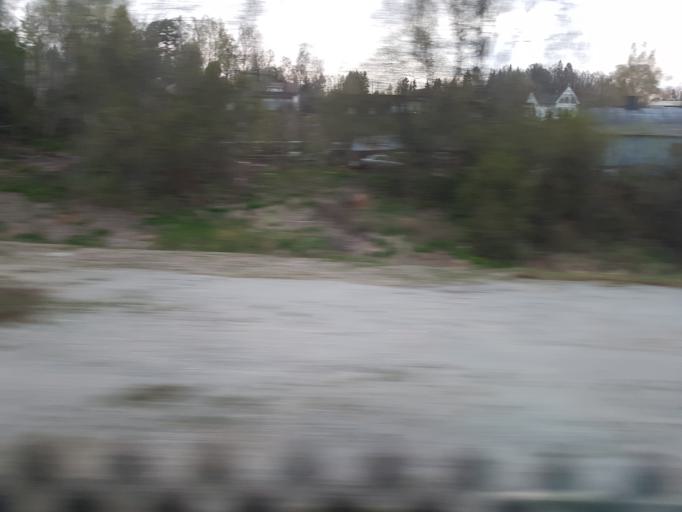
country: NO
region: Hedmark
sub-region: Ringsaker
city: Moelv
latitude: 60.9123
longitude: 10.7379
